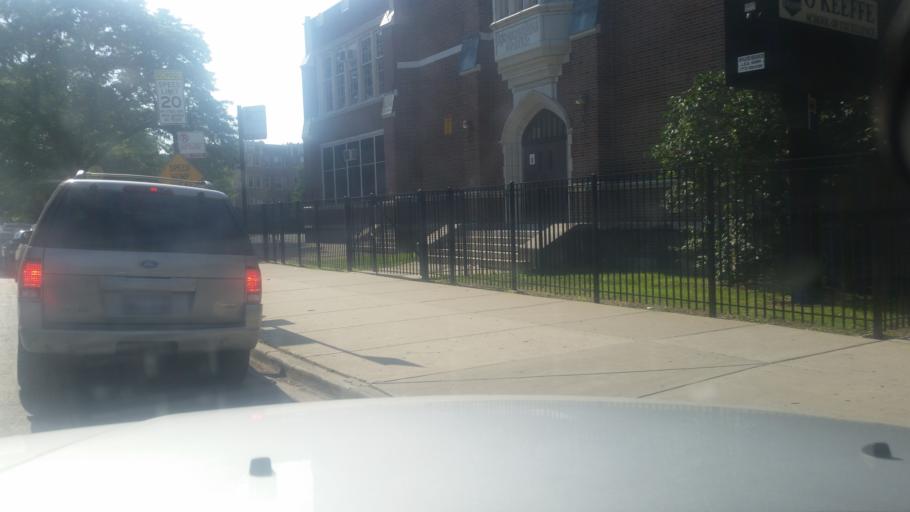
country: US
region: Illinois
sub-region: Cook County
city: Chicago
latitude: 41.7680
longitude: -87.5727
